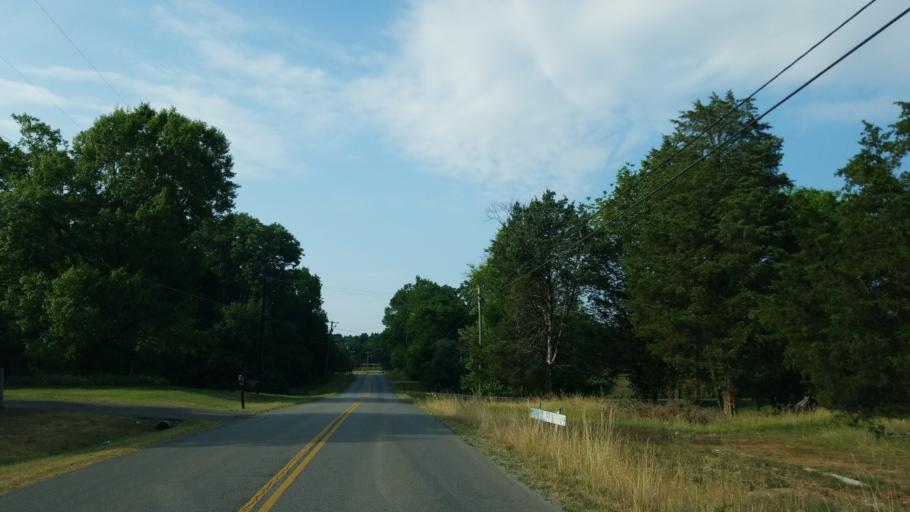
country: US
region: Tennessee
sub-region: Rutherford County
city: La Vergne
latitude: 36.0401
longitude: -86.5859
